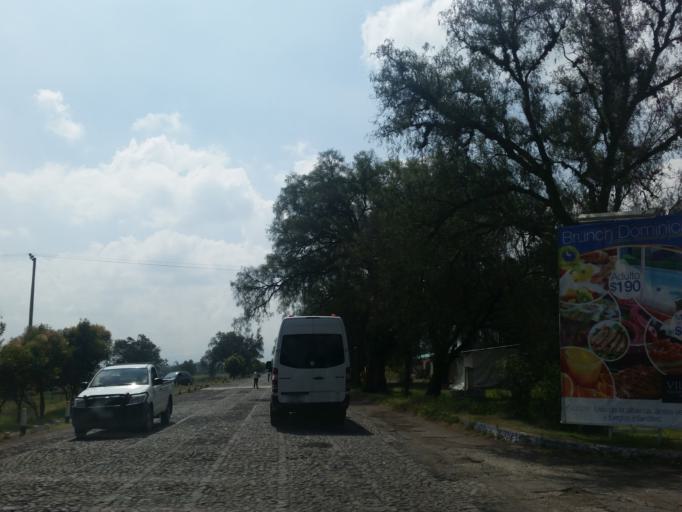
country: MX
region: Morelos
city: Teotihuacan de Arista
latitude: 19.6796
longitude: -98.8505
